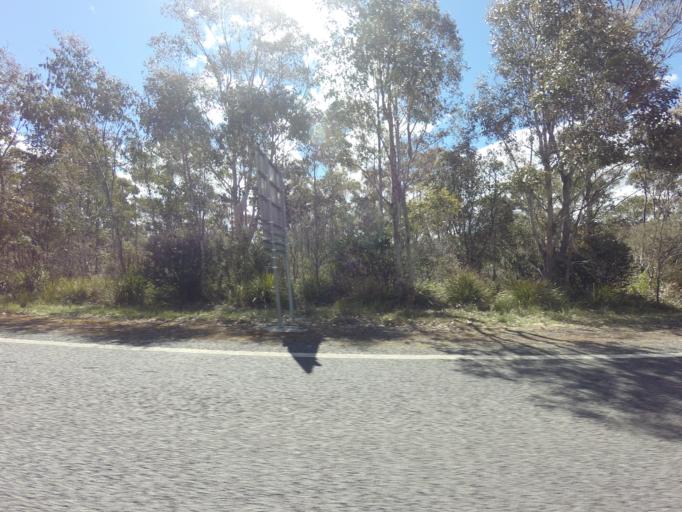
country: AU
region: Tasmania
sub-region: Northern Midlands
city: Evandale
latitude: -42.0245
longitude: 147.8462
